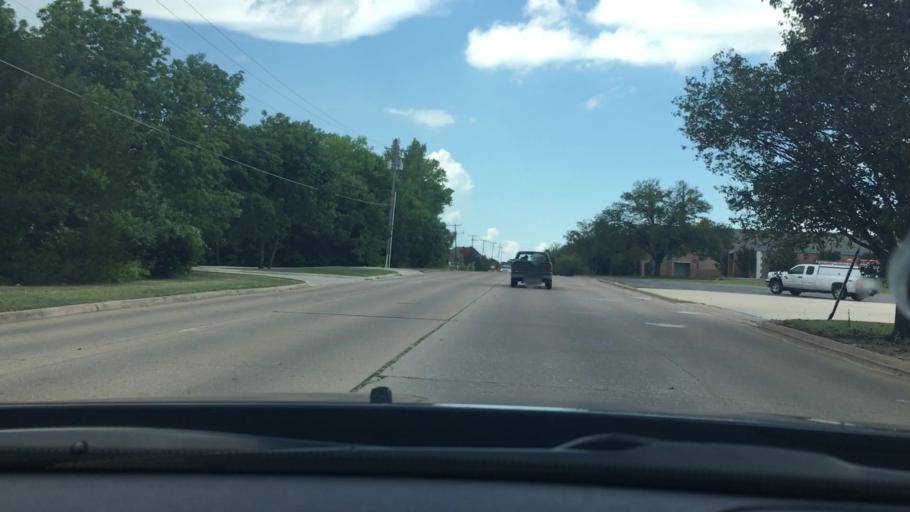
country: US
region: Oklahoma
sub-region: Pontotoc County
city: Ada
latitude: 34.7637
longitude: -96.6612
